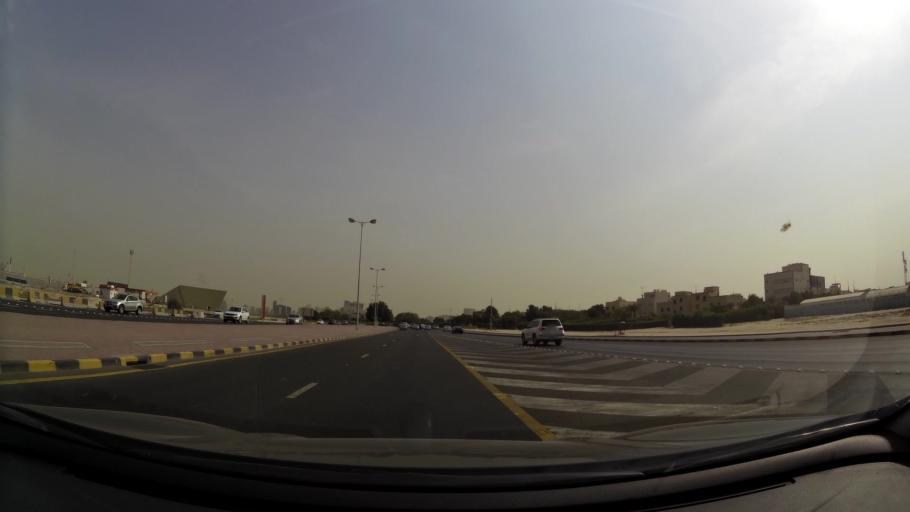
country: KW
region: Al Asimah
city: Ar Rabiyah
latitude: 29.3073
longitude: 47.8940
